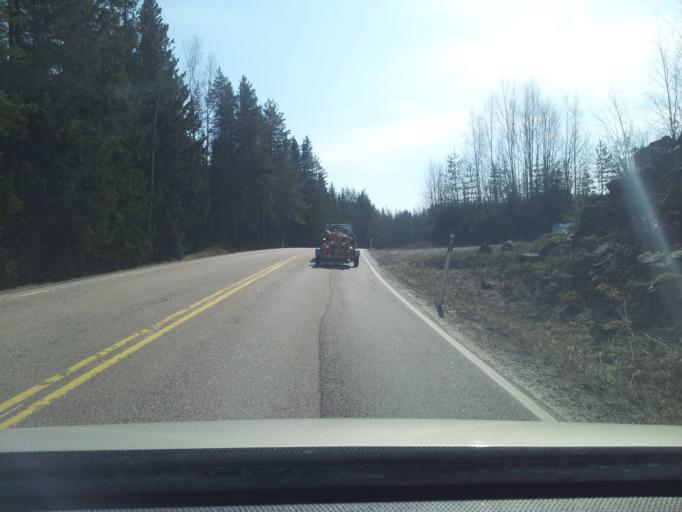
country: FI
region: Kymenlaakso
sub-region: Kotka-Hamina
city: Hamina
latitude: 60.6779
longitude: 27.2763
